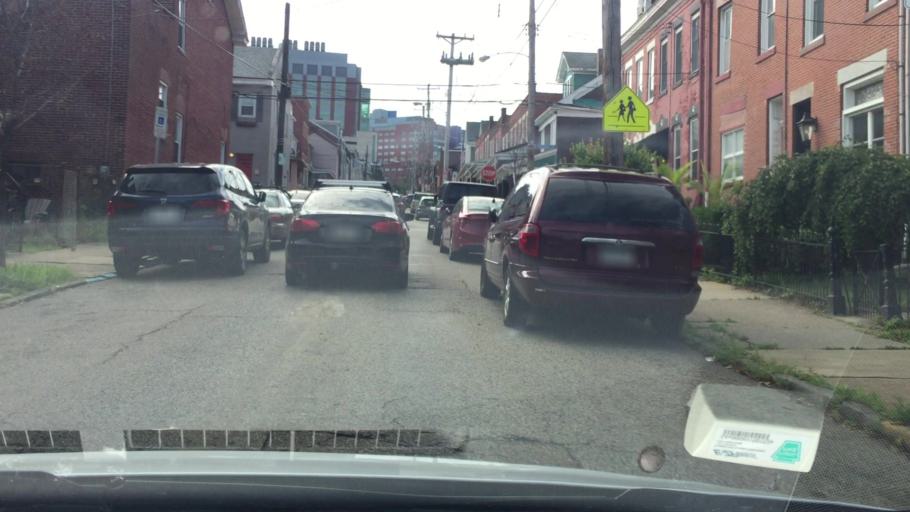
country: US
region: Pennsylvania
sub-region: Allegheny County
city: Bloomfield
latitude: 40.4703
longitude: -79.9582
